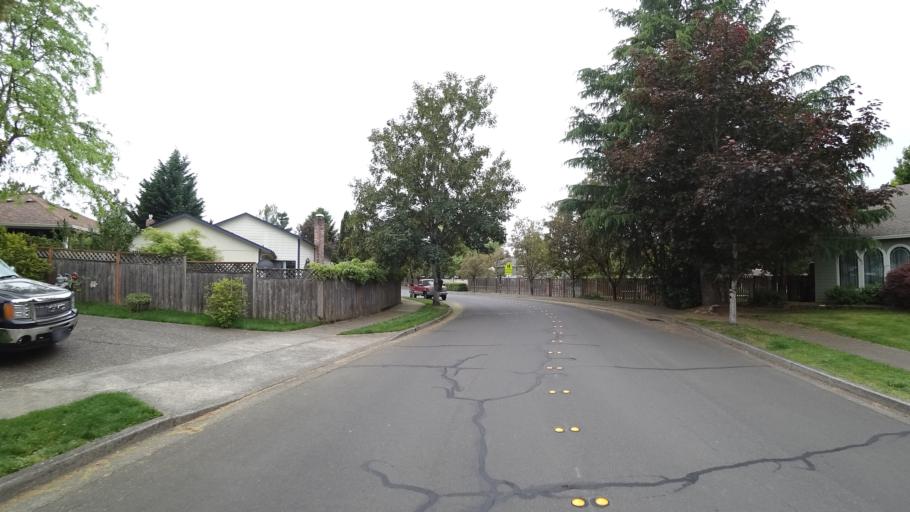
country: US
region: Oregon
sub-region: Washington County
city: Aloha
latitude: 45.5040
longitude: -122.9057
